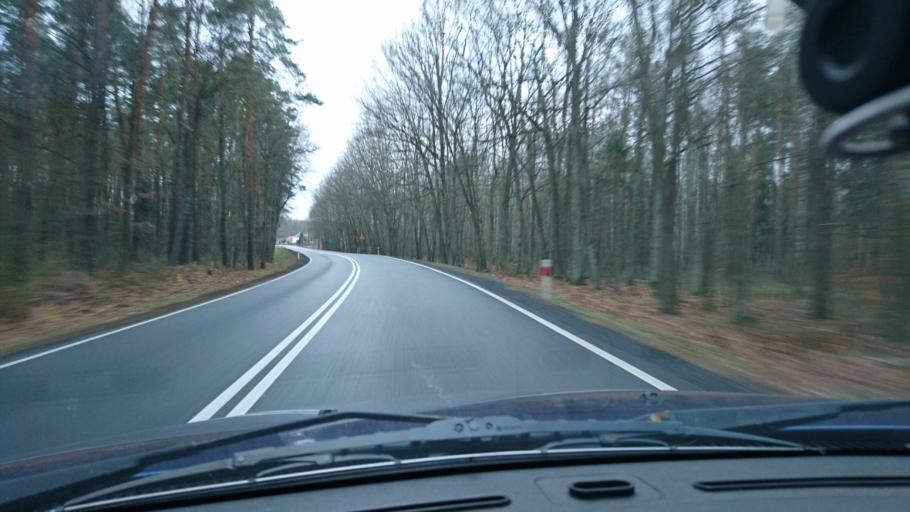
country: PL
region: Opole Voivodeship
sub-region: Powiat kluczborski
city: Kluczbork
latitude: 50.9446
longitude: 18.3215
